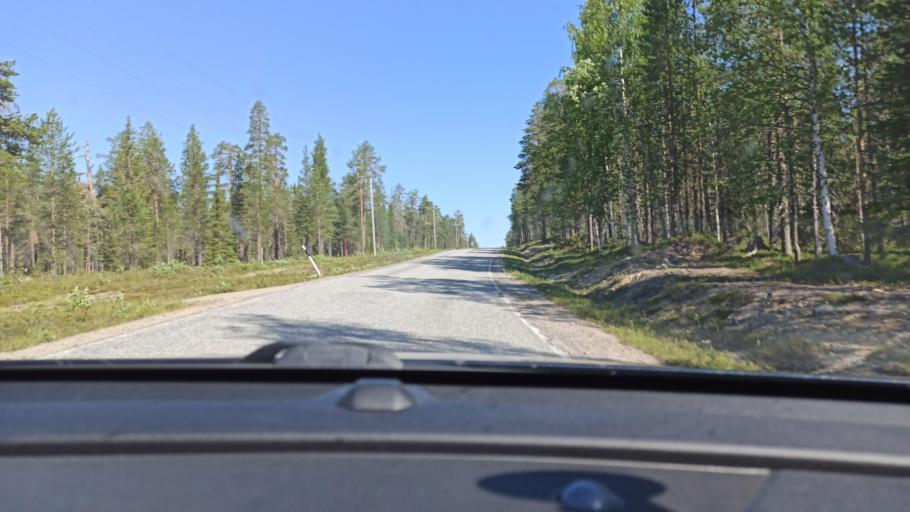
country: FI
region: Lapland
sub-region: Tunturi-Lappi
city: Kolari
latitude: 67.6374
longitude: 24.1564
